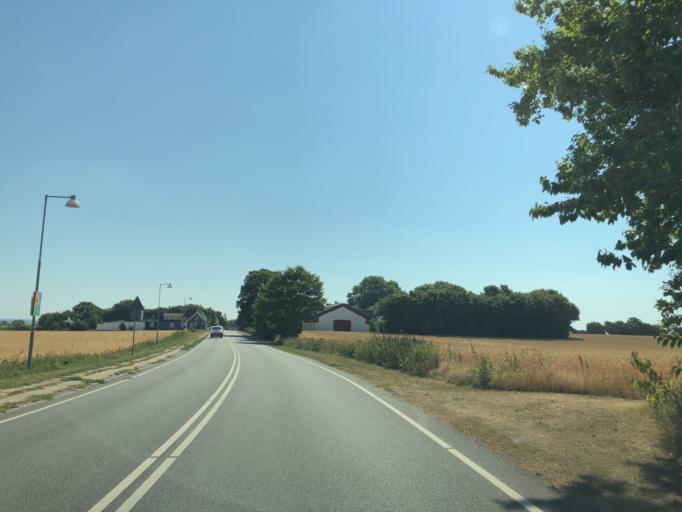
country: DK
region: Zealand
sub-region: Odsherred Kommune
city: Asnaes
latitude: 55.9643
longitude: 11.3713
